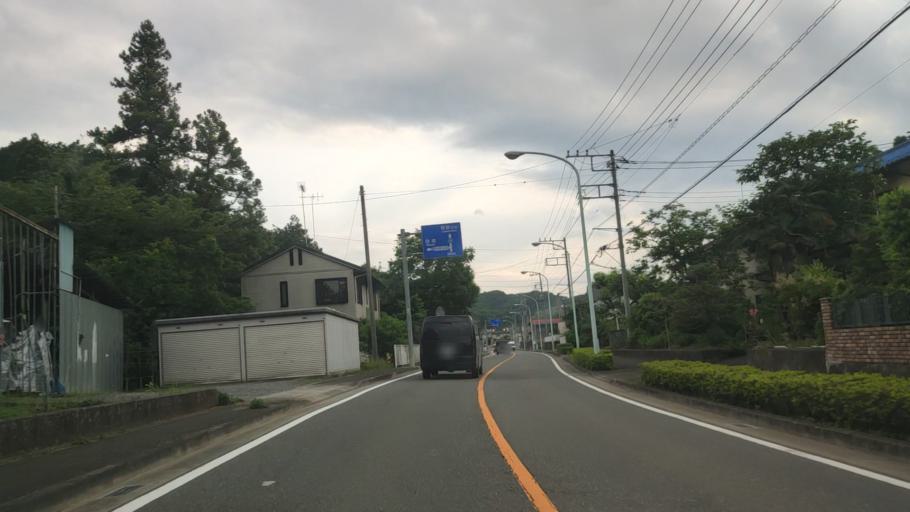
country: JP
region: Saitama
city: Hanno
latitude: 35.8244
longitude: 139.2884
